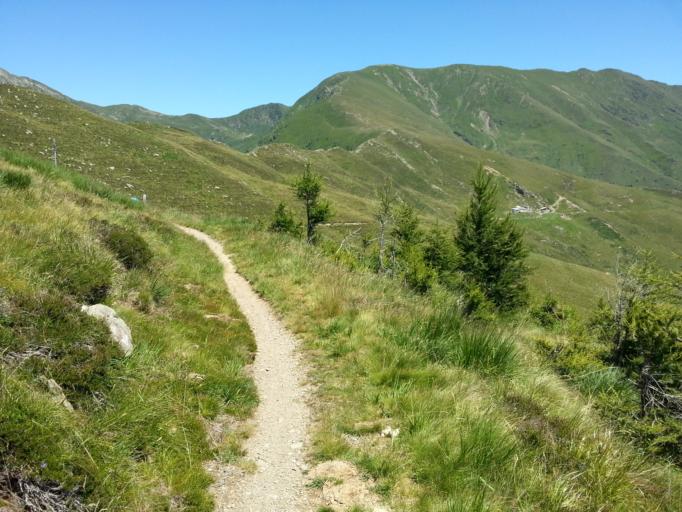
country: CH
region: Ticino
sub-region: Bellinzona District
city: Camorino
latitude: 46.1108
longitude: 9.0396
